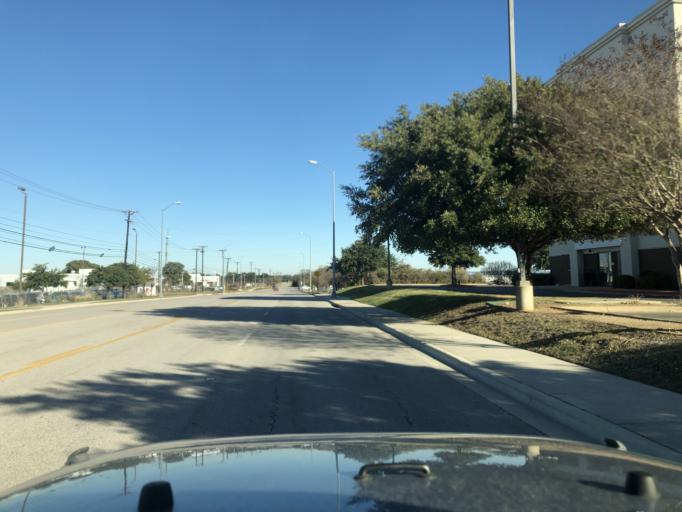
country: US
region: Texas
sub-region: Williamson County
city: Round Rock
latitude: 30.5405
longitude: -97.6949
